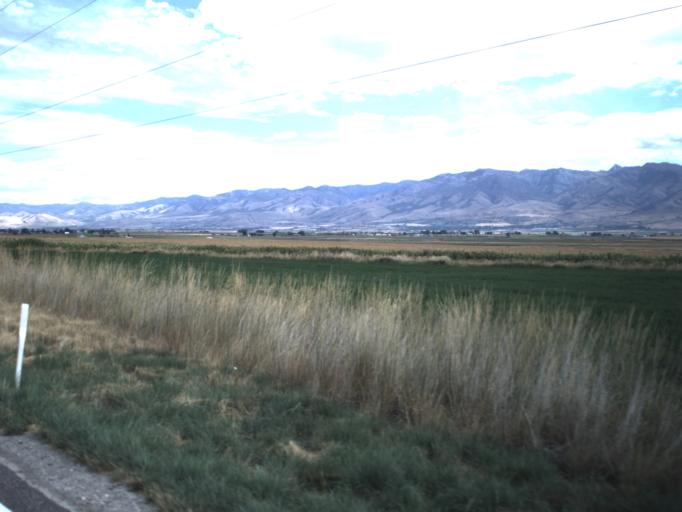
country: US
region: Utah
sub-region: Cache County
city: Benson
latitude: 41.8707
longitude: -111.9503
